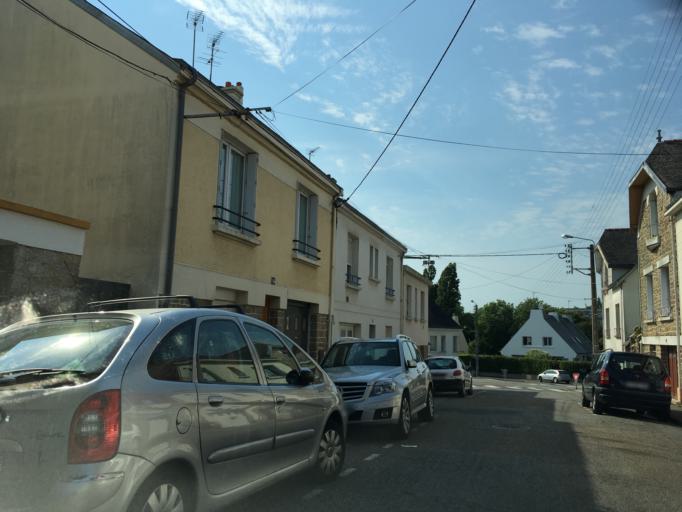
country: FR
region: Brittany
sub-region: Departement du Morbihan
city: Lorient
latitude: 47.7616
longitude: -3.3795
